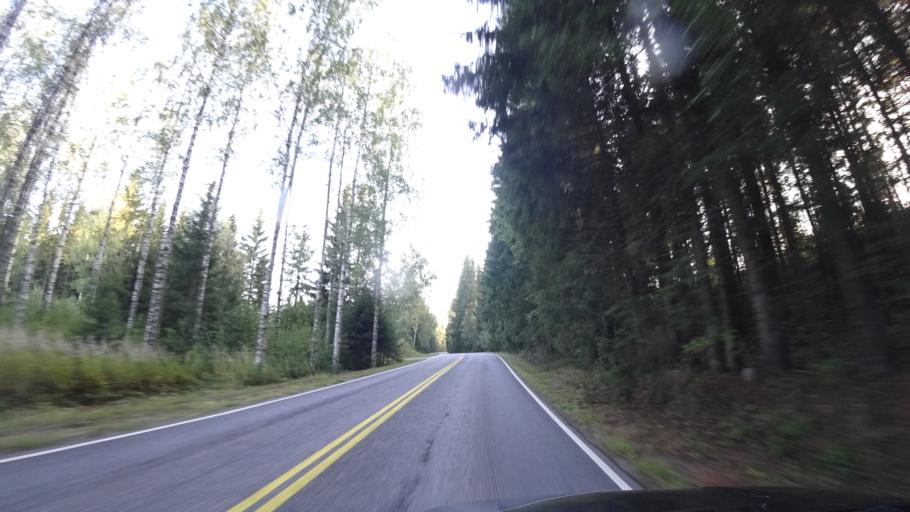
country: FI
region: Haeme
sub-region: Haemeenlinna
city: Tuulos
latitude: 61.0012
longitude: 24.8373
